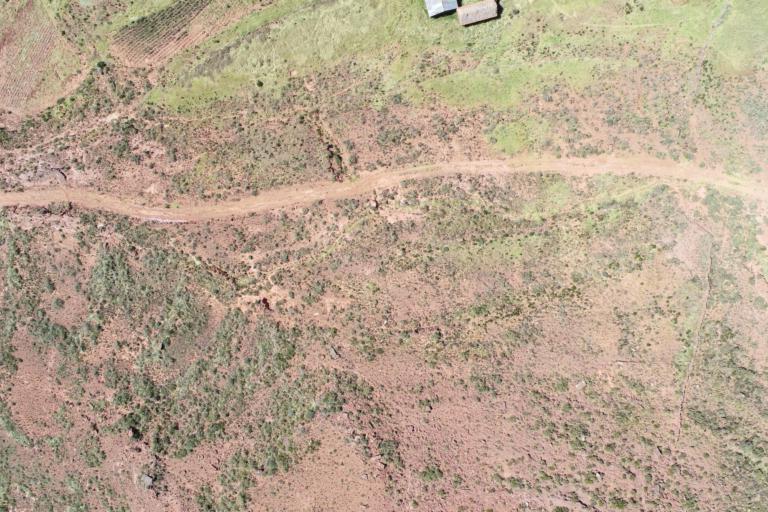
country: BO
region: La Paz
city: Tiahuanaco
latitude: -16.6056
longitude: -68.7691
